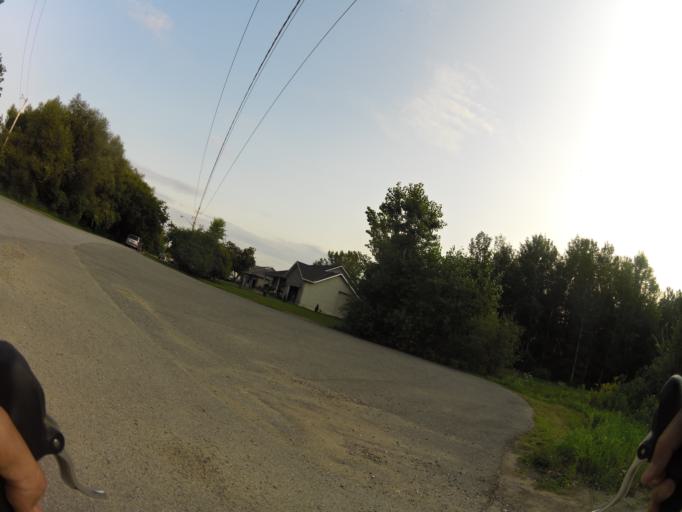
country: CA
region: Ontario
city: Bells Corners
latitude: 45.3502
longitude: -75.9037
